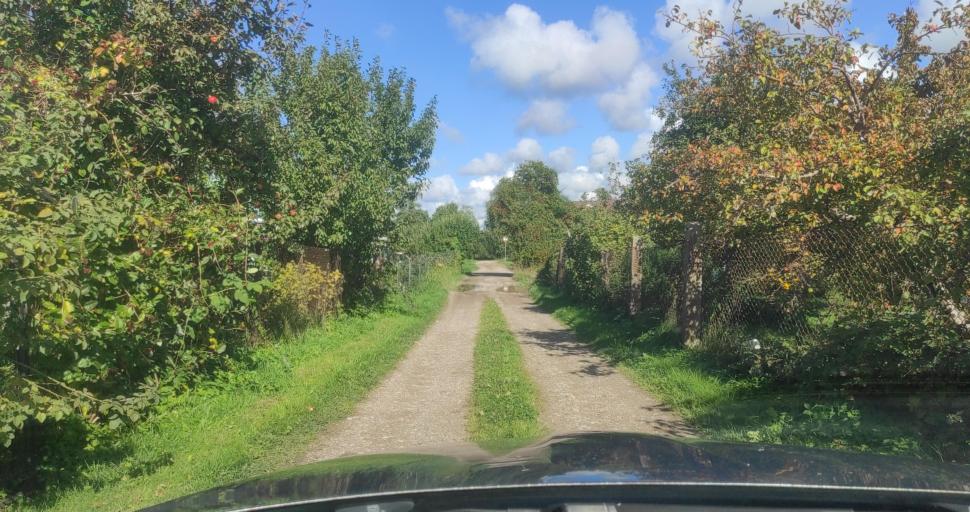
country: LV
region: Ventspils
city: Ventspils
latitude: 57.3708
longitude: 21.6059
